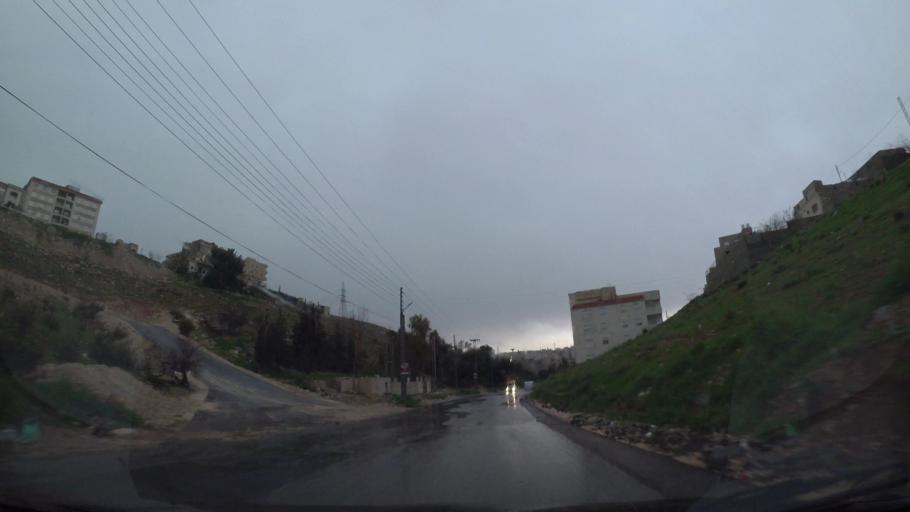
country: JO
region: Amman
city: Amman
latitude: 31.9931
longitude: 35.9724
